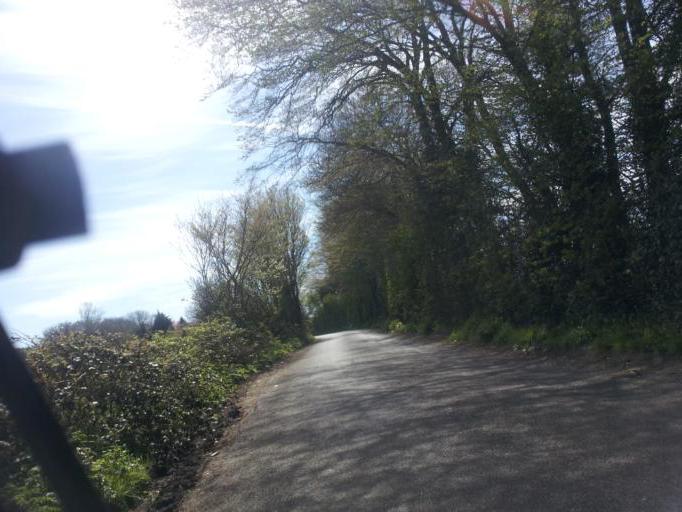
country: GB
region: England
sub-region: Kent
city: Rainham
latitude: 51.3101
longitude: 0.6107
